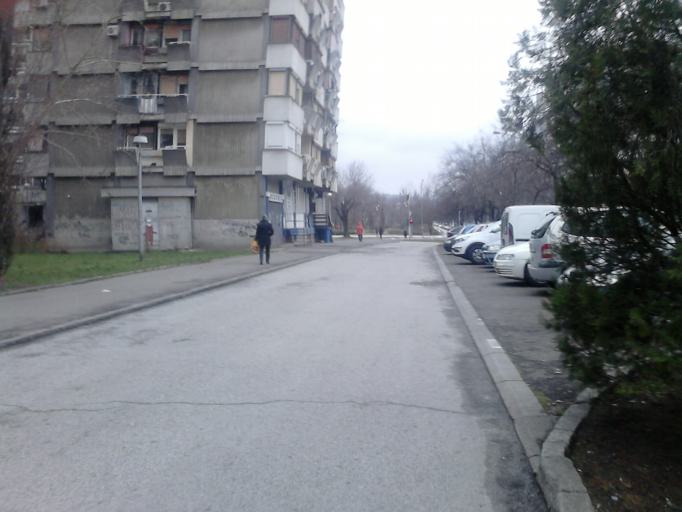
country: RS
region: Autonomna Pokrajina Vojvodina
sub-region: Juznobacki Okrug
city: Novi Sad
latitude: 45.2414
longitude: 19.8375
